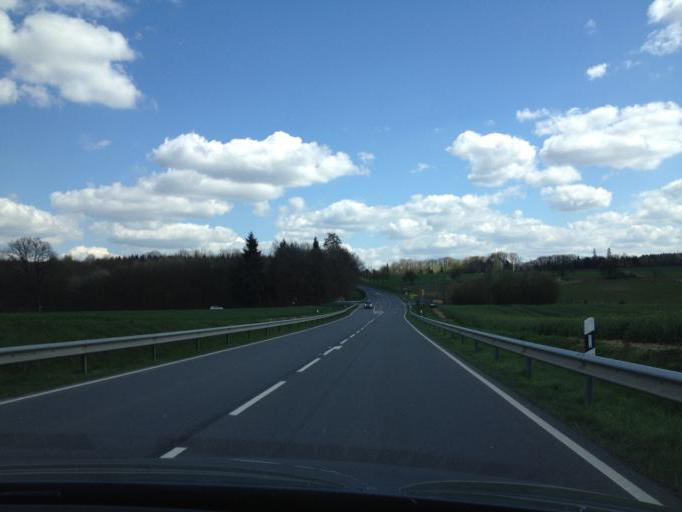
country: DE
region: Baden-Wuerttemberg
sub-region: Karlsruhe Region
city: Osterburken
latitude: 49.4137
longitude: 9.4564
